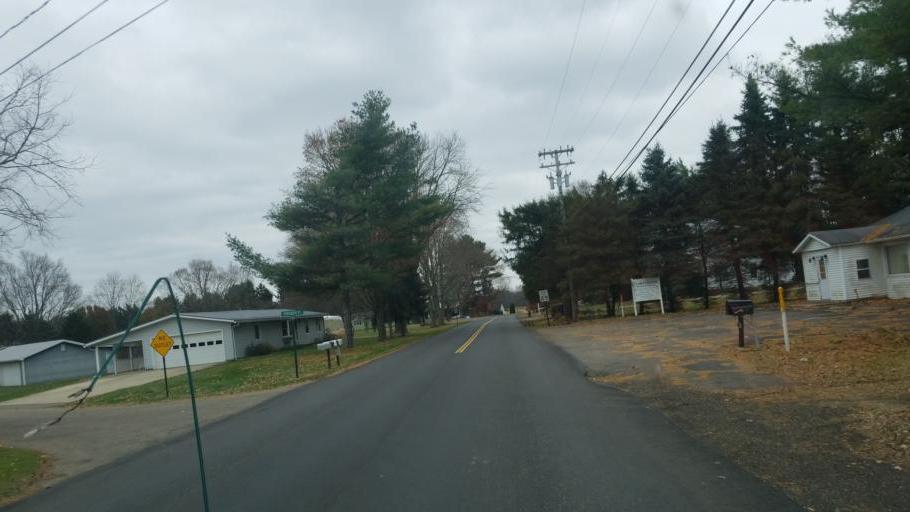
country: US
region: Ohio
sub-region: Knox County
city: Fredericktown
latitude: 40.4784
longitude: -82.5375
